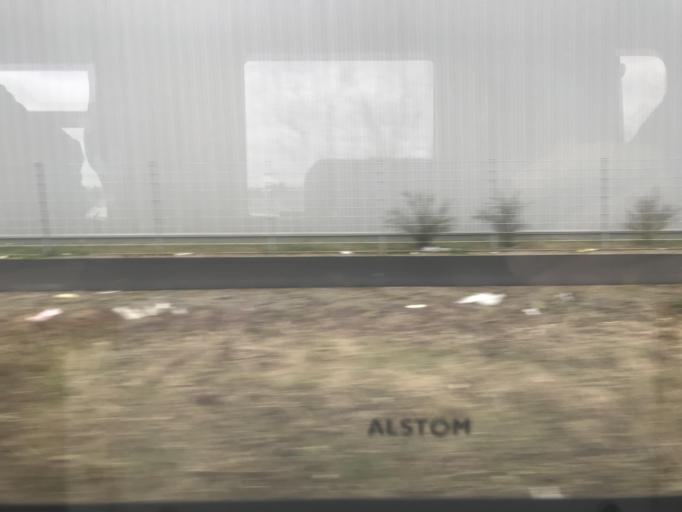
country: DE
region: Hesse
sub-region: Regierungsbezirk Darmstadt
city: Gross-Gerau
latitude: 49.9281
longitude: 8.4751
